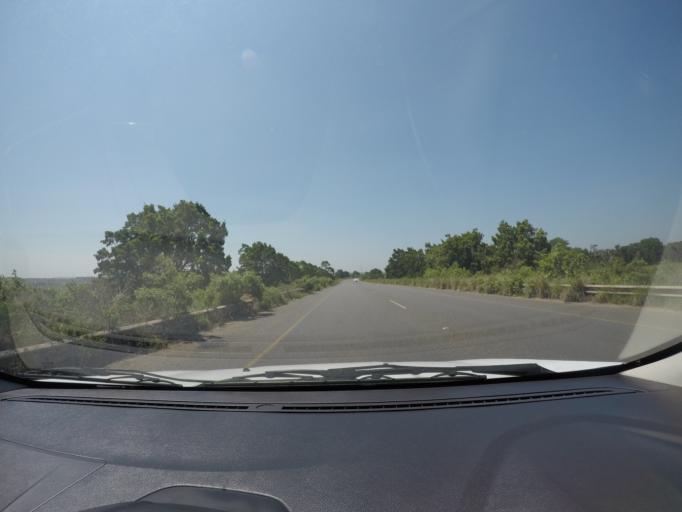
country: ZA
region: KwaZulu-Natal
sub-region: uThungulu District Municipality
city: Empangeni
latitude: -28.7800
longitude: 31.9580
